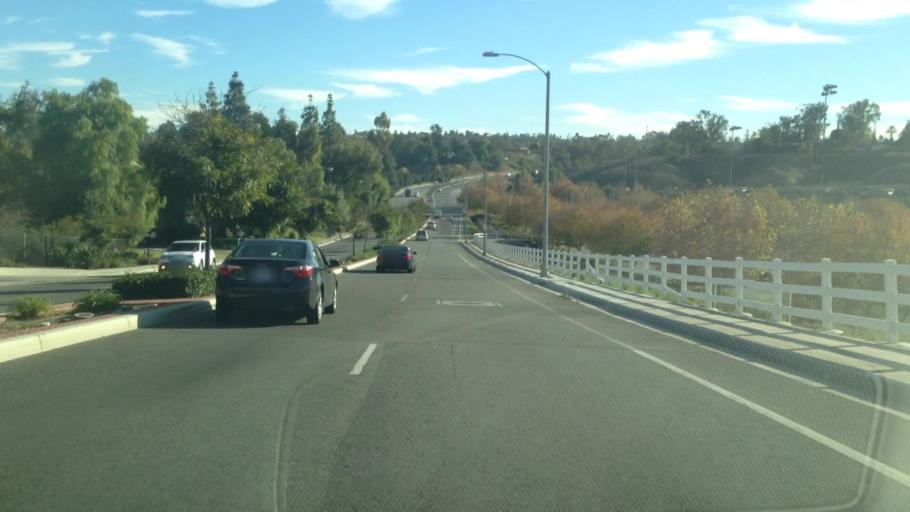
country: US
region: California
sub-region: Riverside County
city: Riverside
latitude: 33.9595
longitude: -117.3478
